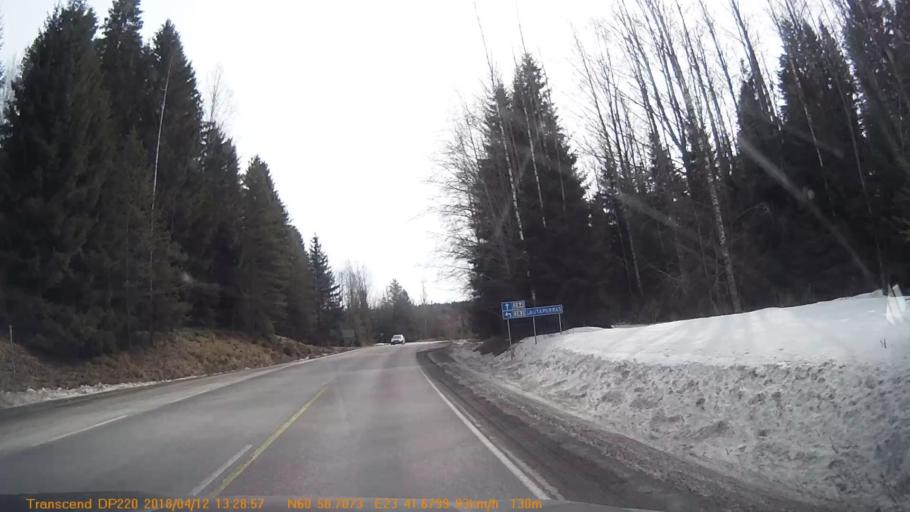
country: FI
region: Pirkanmaa
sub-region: Etelae-Pirkanmaa
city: Kylmaekoski
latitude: 60.9782
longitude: 23.6949
